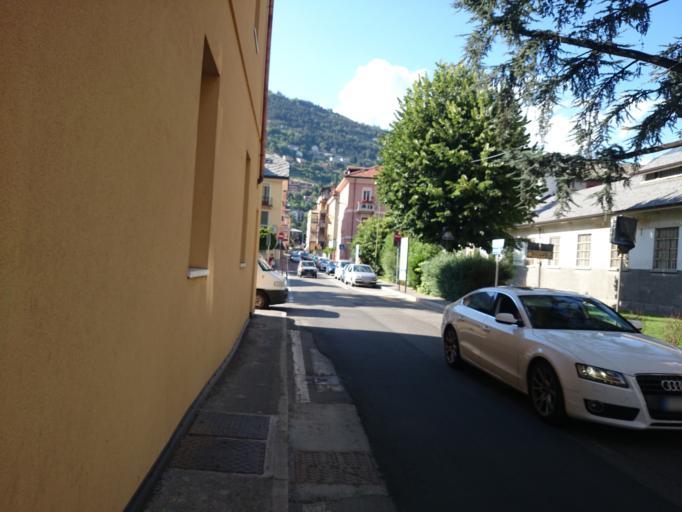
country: IT
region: Aosta Valley
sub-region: Valle d'Aosta
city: Aosta
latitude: 45.7359
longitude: 7.3126
